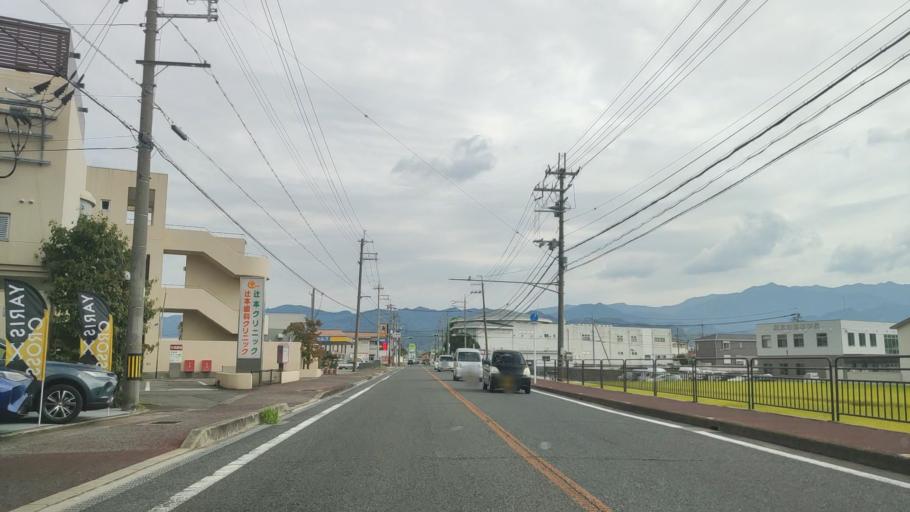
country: JP
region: Wakayama
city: Hashimoto
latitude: 34.3048
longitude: 135.5483
